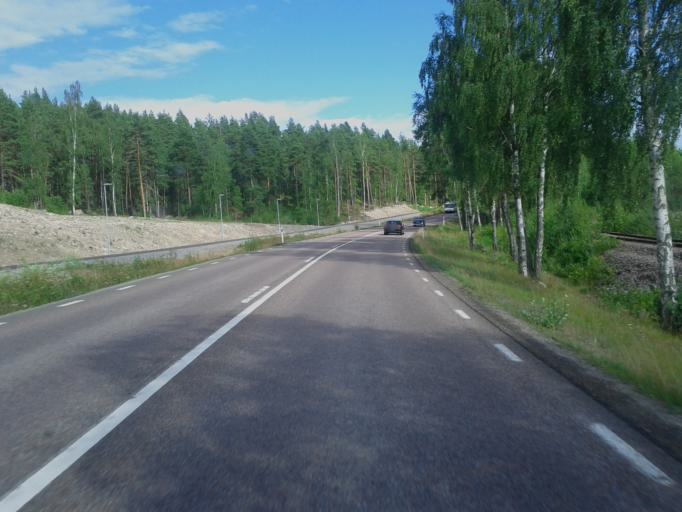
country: SE
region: Dalarna
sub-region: Faluns Kommun
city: Grycksbo
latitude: 60.6711
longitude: 15.5319
